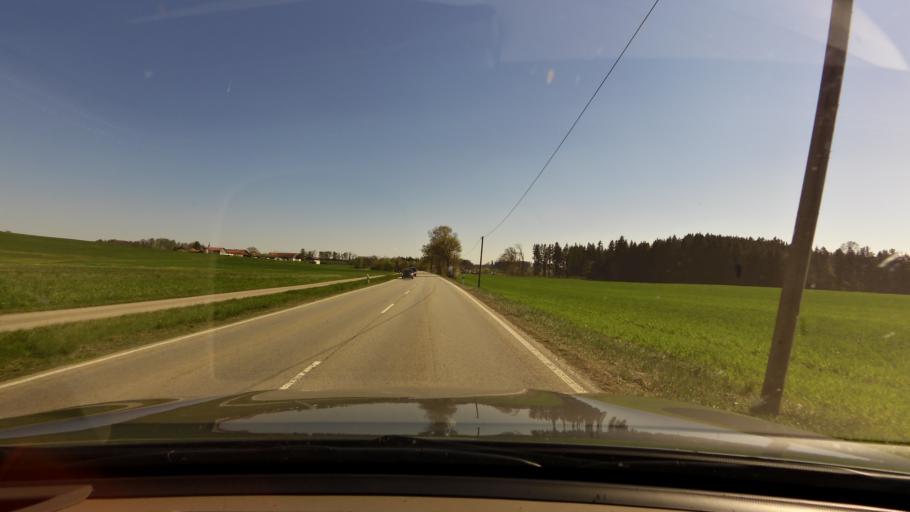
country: DE
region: Bavaria
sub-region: Upper Bavaria
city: Soyen
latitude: 48.1016
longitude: 12.1906
